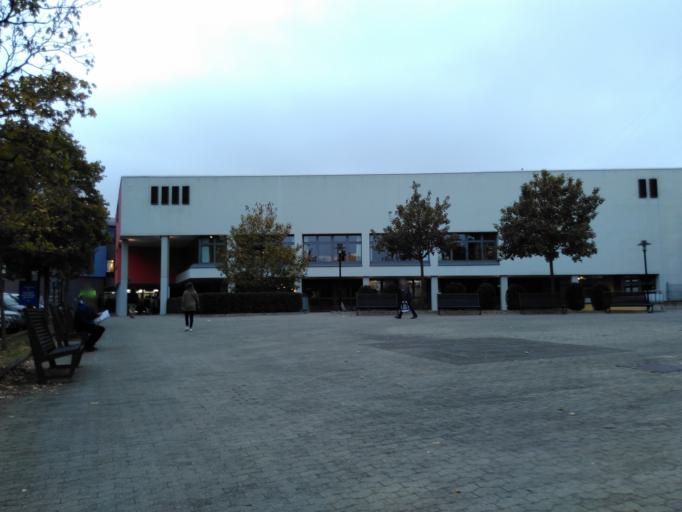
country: CH
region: Zurich
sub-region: Bezirk Buelach
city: Kloten / Spitz
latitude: 47.4447
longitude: 8.5818
